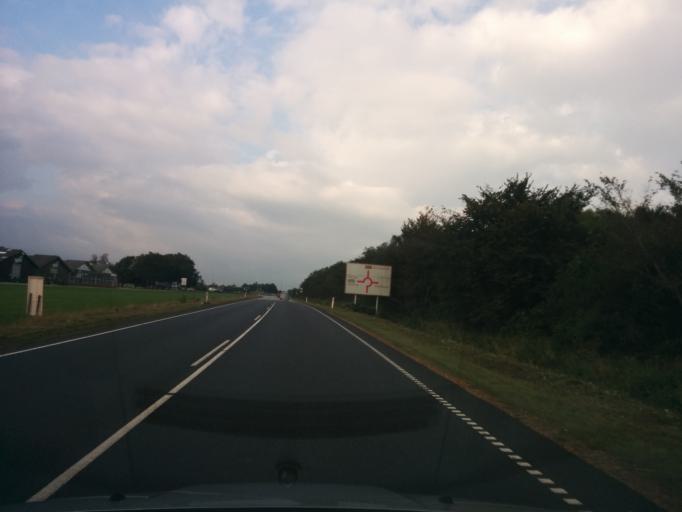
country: DK
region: South Denmark
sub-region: Billund Kommune
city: Grindsted
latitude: 55.6497
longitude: 8.8129
